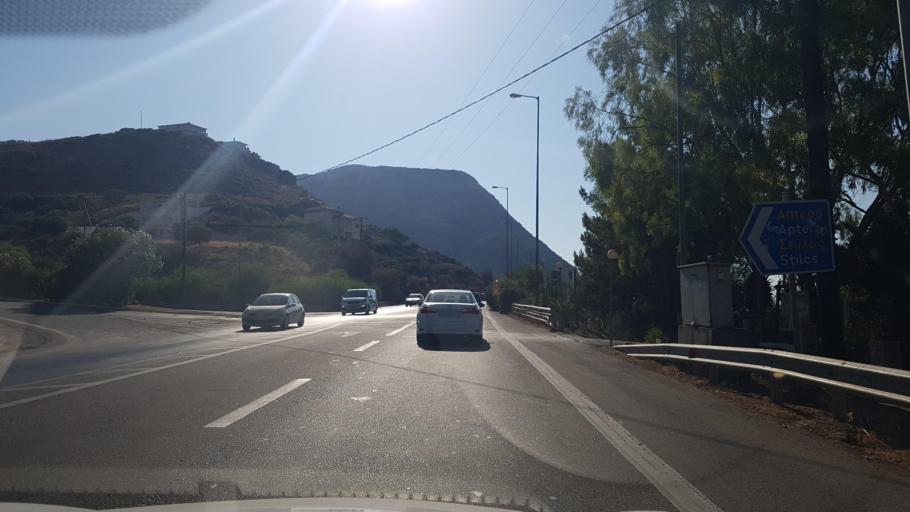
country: GR
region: Crete
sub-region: Nomos Chanias
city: Kalivai
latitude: 35.4686
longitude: 24.1260
